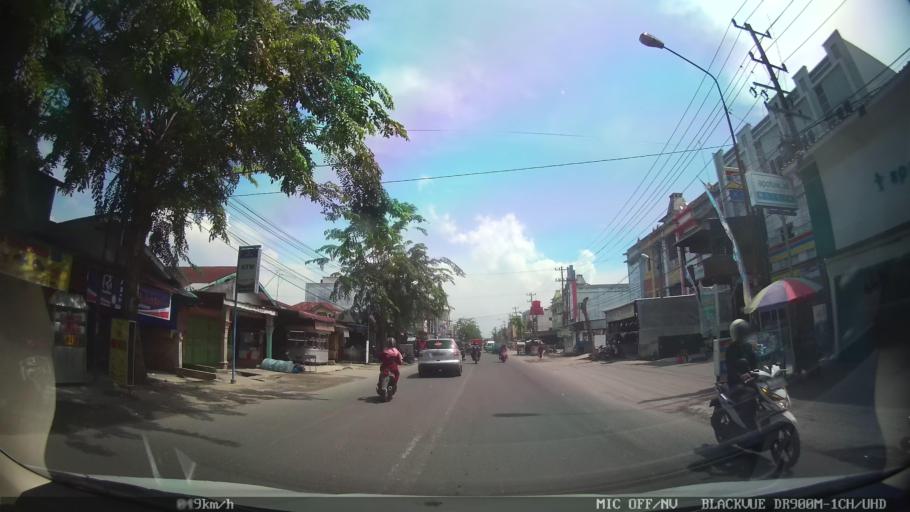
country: ID
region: North Sumatra
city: Labuhan Deli
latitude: 3.6846
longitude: 98.6561
